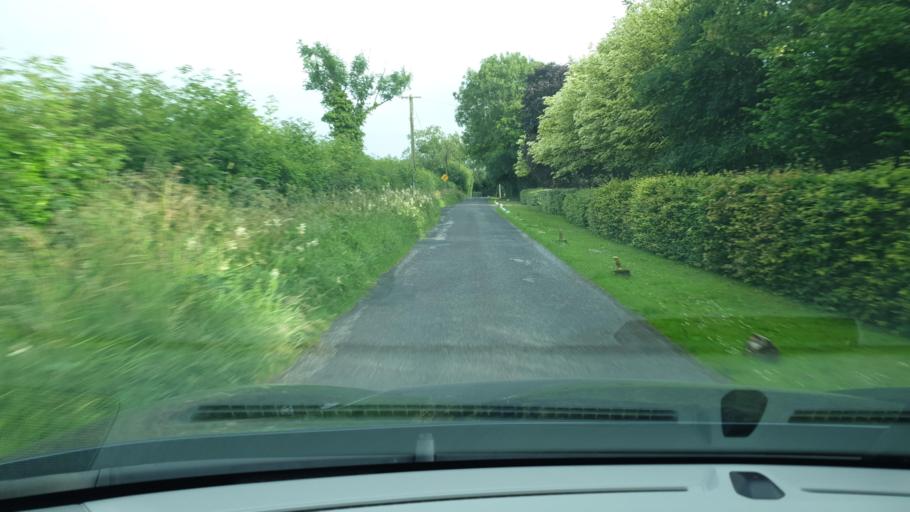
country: IE
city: Confey
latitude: 53.4047
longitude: -6.5095
